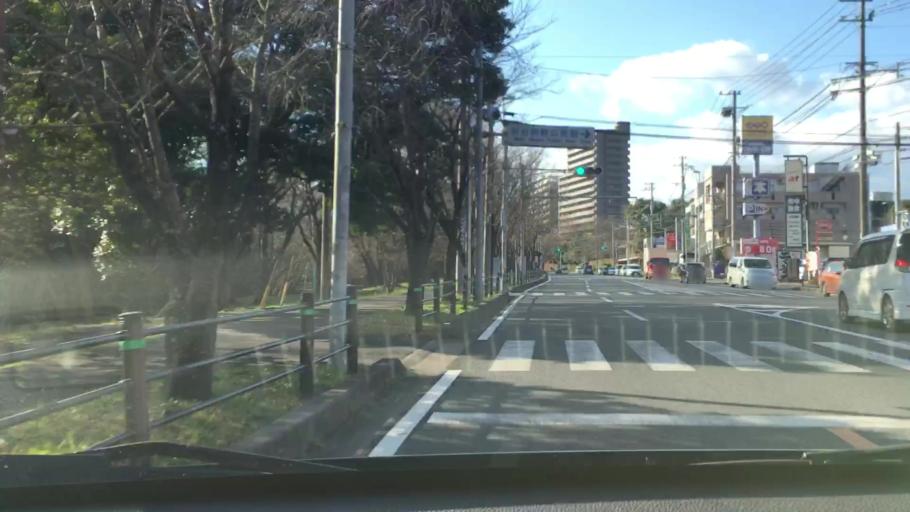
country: JP
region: Oita
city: Tsurusaki
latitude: 33.2253
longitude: 131.6582
